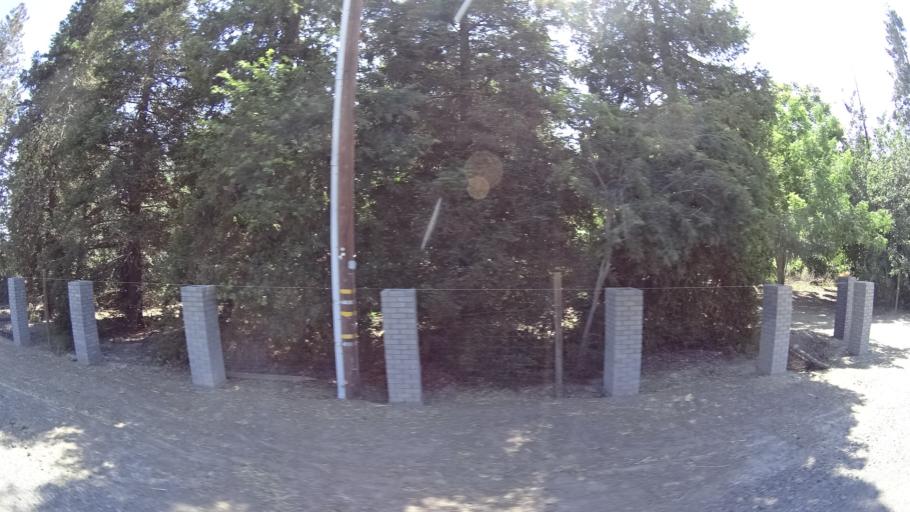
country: US
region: California
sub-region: Fresno County
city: Riverdale
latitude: 36.3734
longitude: -119.8513
